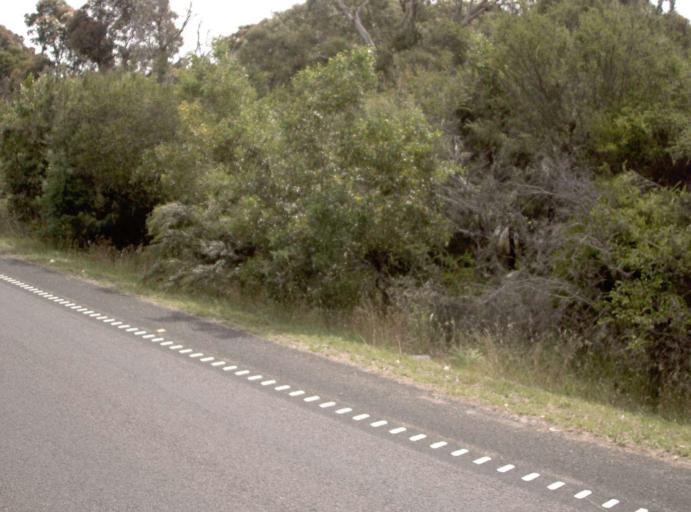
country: AU
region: Victoria
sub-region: Mornington Peninsula
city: Moorooduc
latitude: -38.2178
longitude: 145.1065
